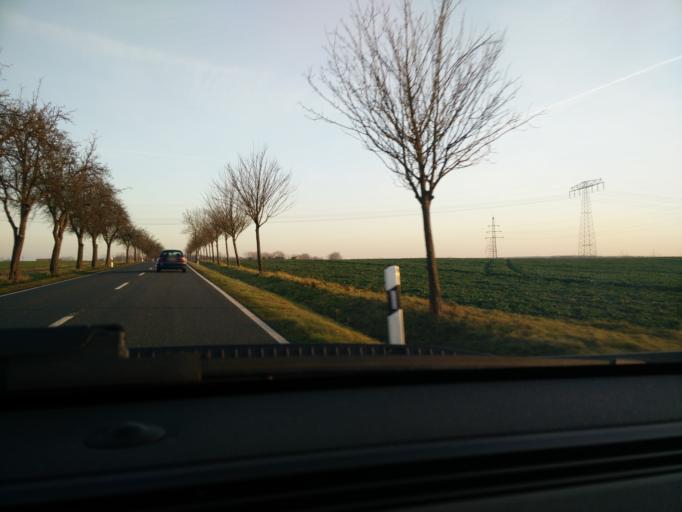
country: DE
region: Saxony
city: Kitzscher
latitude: 51.1670
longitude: 12.5356
